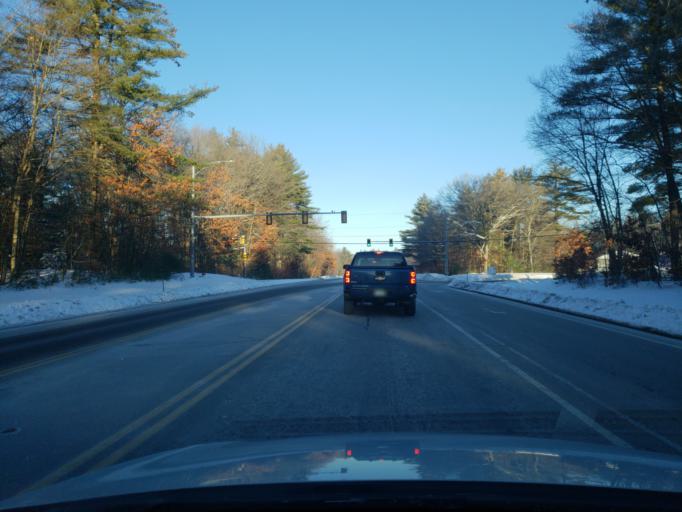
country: US
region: New Hampshire
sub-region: Hillsborough County
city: Pinardville
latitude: 42.9739
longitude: -71.5145
